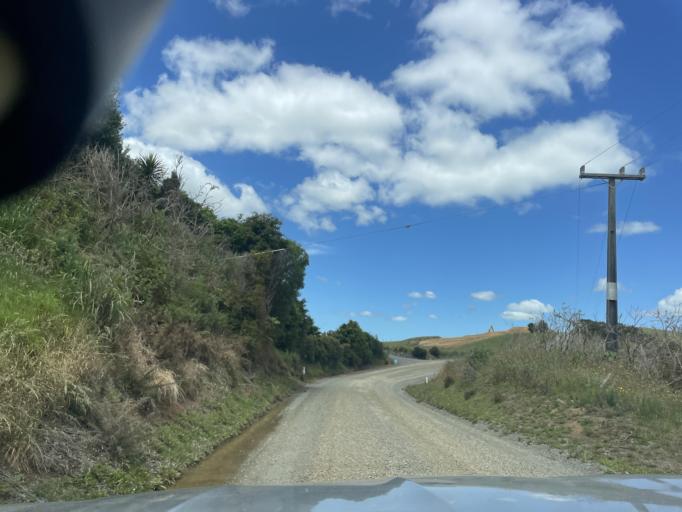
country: NZ
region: Auckland
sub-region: Auckland
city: Wellsford
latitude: -36.1559
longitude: 174.5424
